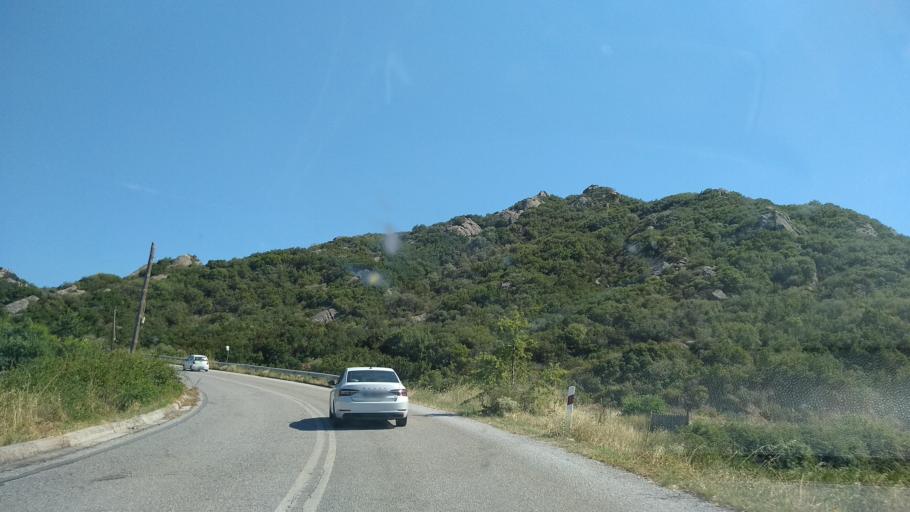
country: GR
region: Central Macedonia
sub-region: Nomos Chalkidikis
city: Sykia
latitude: 40.0335
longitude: 23.9821
